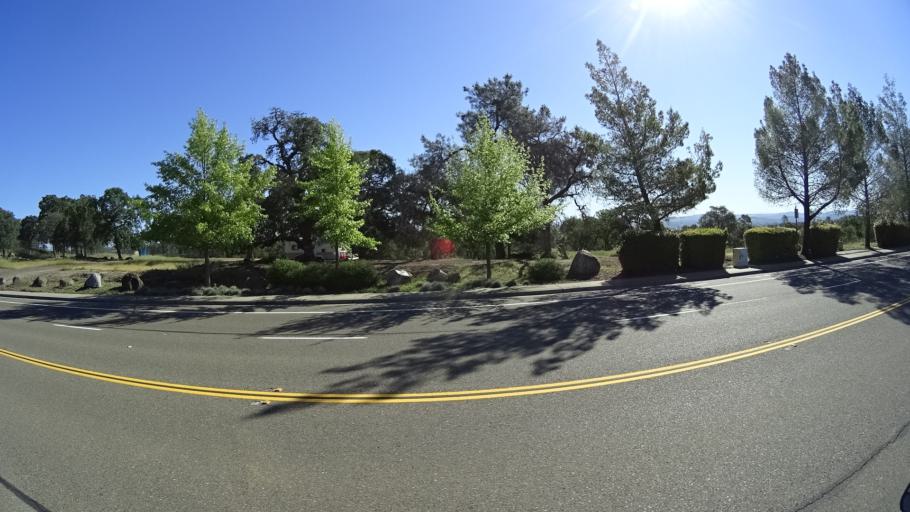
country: US
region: California
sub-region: Placer County
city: Loomis
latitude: 38.8362
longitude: -121.2299
